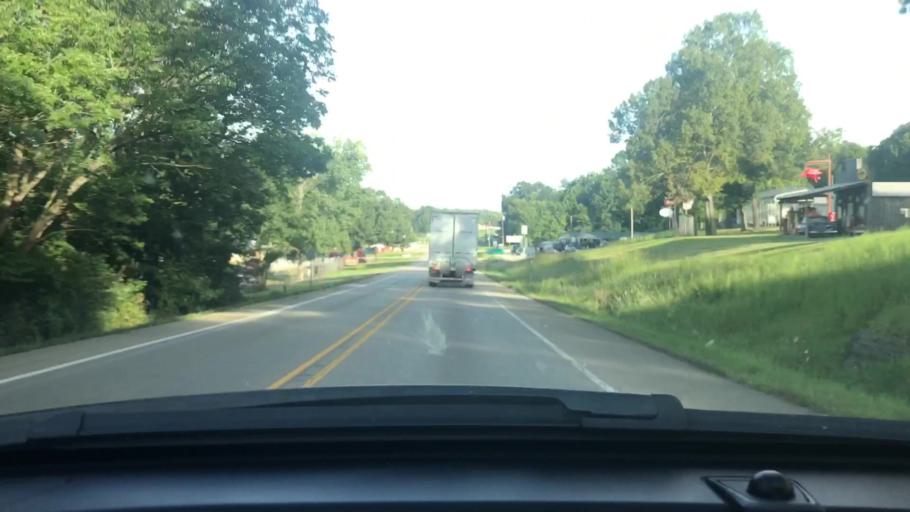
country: US
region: Arkansas
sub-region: Sharp County
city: Cherokee Village
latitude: 36.2379
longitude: -91.2565
